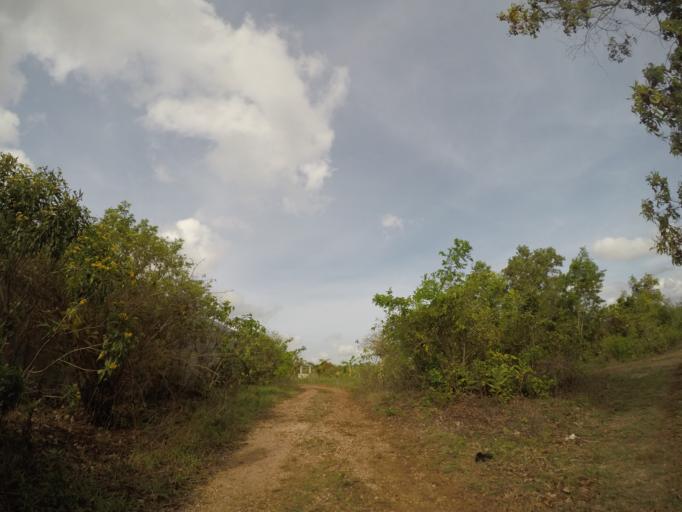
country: TZ
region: Zanzibar Central/South
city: Koani
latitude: -6.2343
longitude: 39.3185
